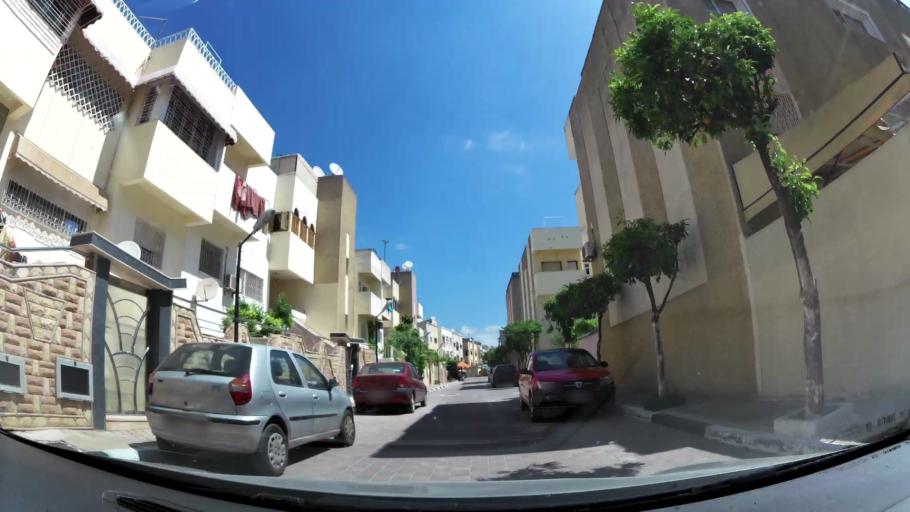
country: MA
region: Fes-Boulemane
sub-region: Fes
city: Fes
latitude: 34.0241
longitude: -5.0182
